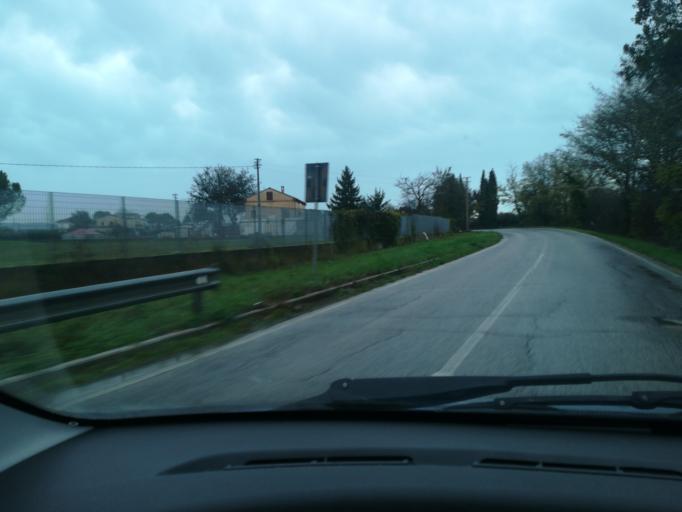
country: IT
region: The Marches
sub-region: Provincia di Macerata
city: Trodica
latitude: 43.2774
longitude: 13.6149
